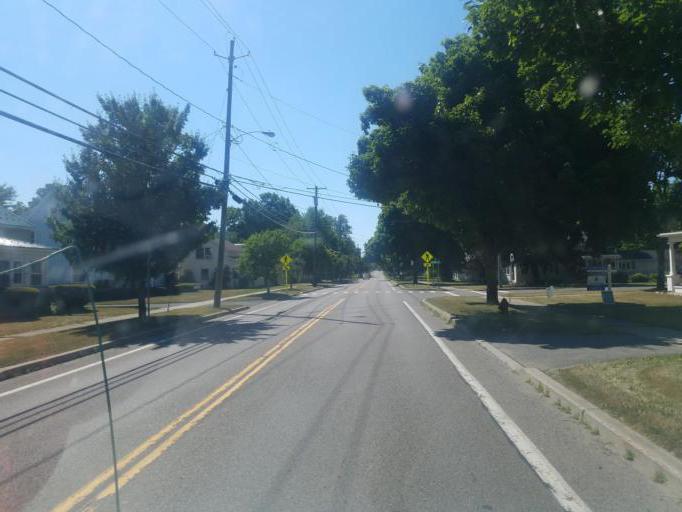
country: US
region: New York
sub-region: Ontario County
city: Phelps
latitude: 42.9604
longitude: -77.0670
